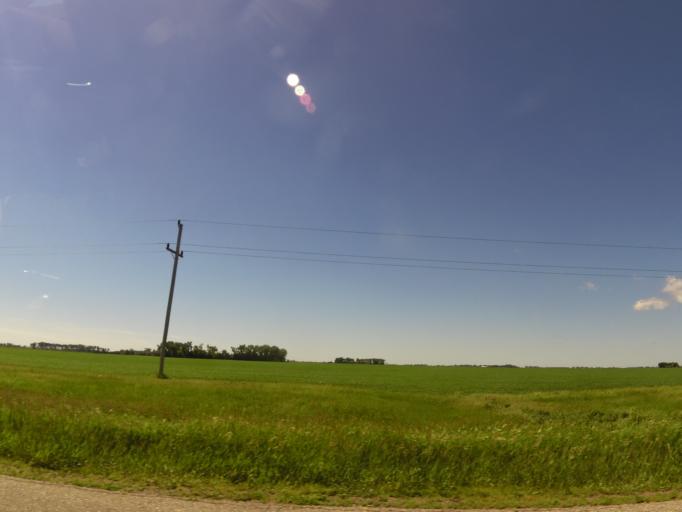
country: US
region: Minnesota
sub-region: Polk County
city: Crookston
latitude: 47.7604
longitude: -96.5080
